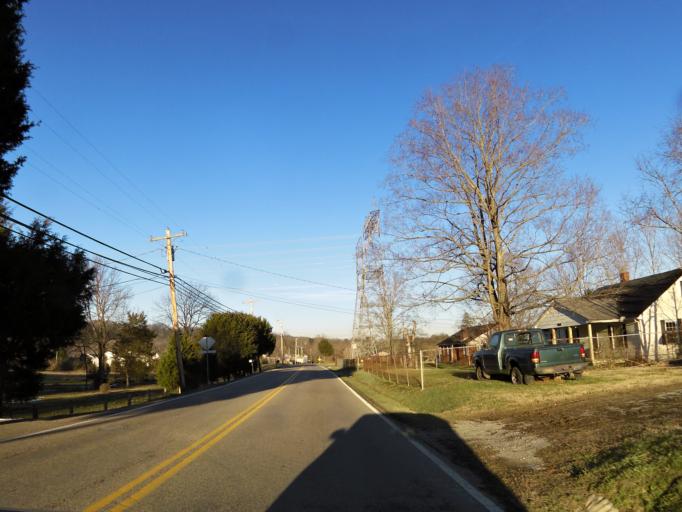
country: US
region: Tennessee
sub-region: Knox County
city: Farragut
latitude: 35.9579
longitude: -84.1125
